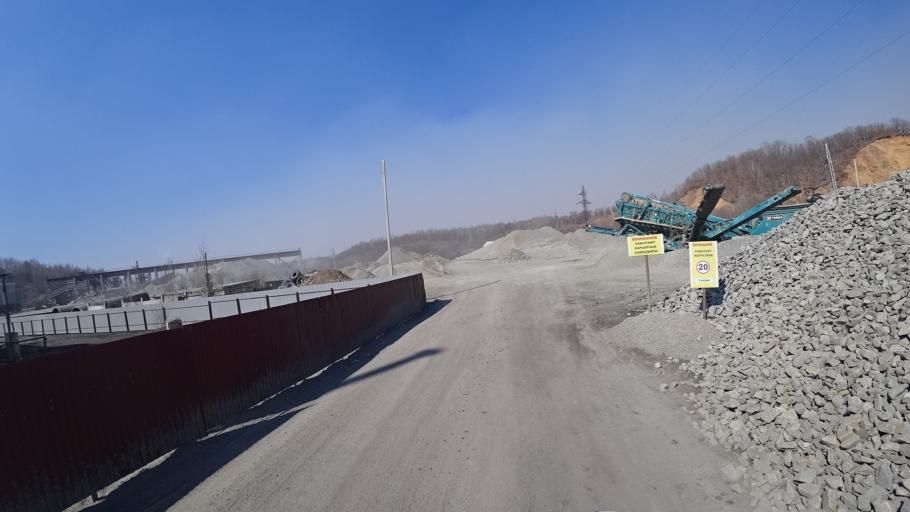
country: RU
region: Amur
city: Novobureyskiy
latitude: 49.7910
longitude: 129.9621
